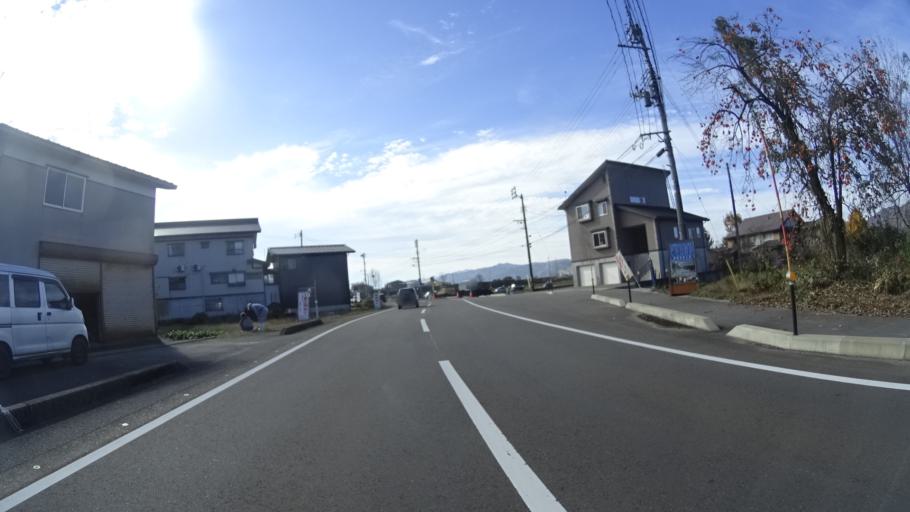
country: JP
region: Niigata
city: Ojiya
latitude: 37.2414
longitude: 138.9805
